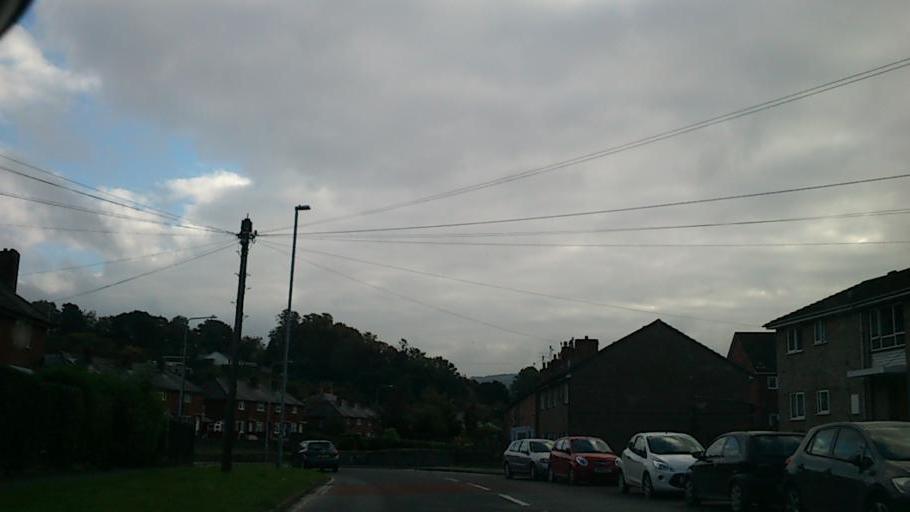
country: GB
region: Wales
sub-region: Sir Powys
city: Welshpool
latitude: 52.6618
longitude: -3.1522
